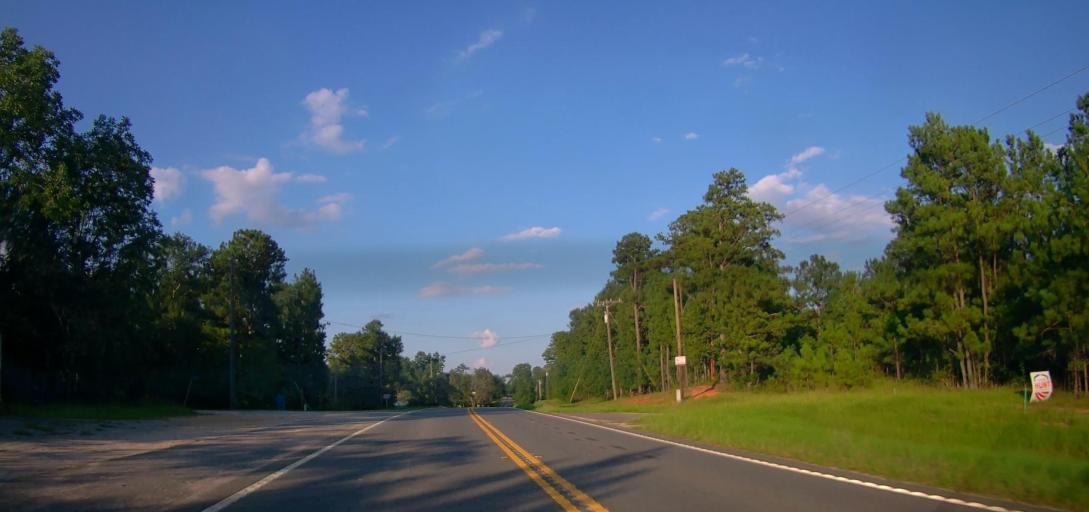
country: US
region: Georgia
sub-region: Crawford County
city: Roberta
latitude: 32.7078
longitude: -84.0315
